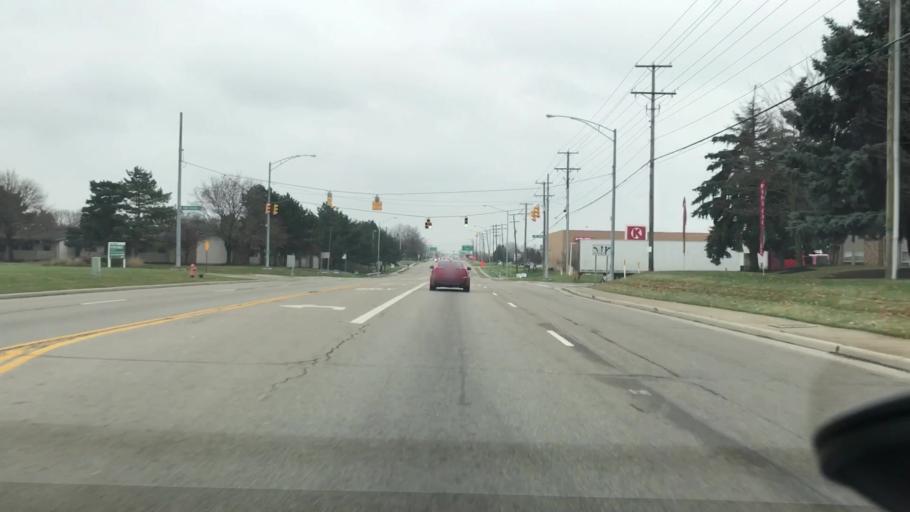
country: US
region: Ohio
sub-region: Franklin County
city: Lincoln Village
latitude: 39.9802
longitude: -83.1032
